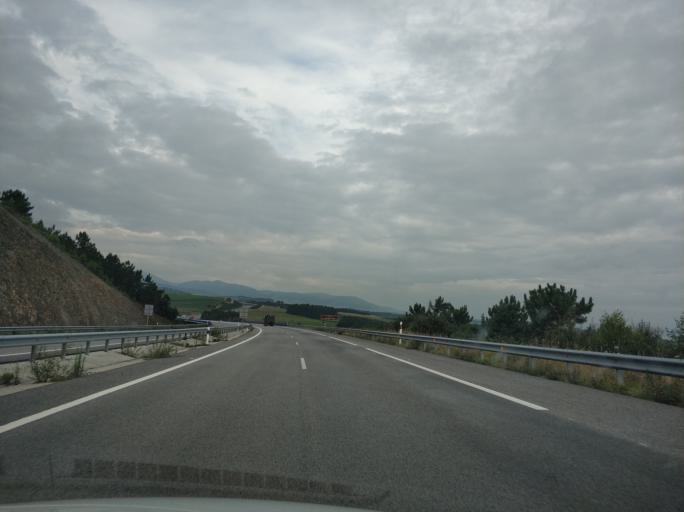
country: ES
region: Asturias
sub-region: Province of Asturias
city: Navia
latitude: 43.5410
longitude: -6.6279
